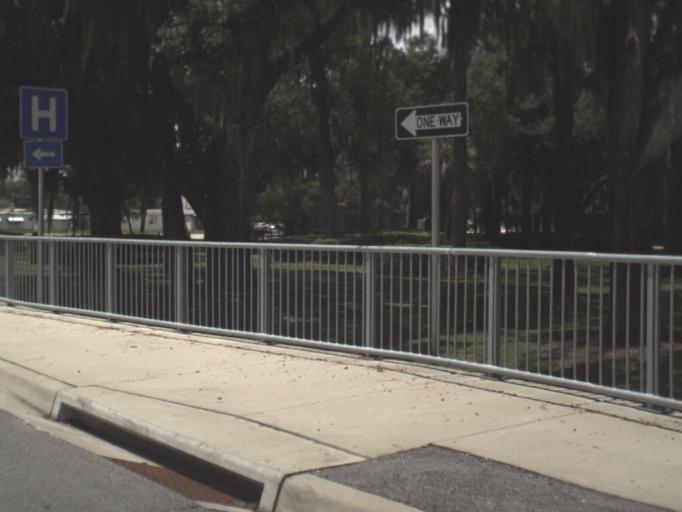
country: US
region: Florida
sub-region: Hillsborough County
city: Plant City
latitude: 28.0177
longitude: -82.1370
